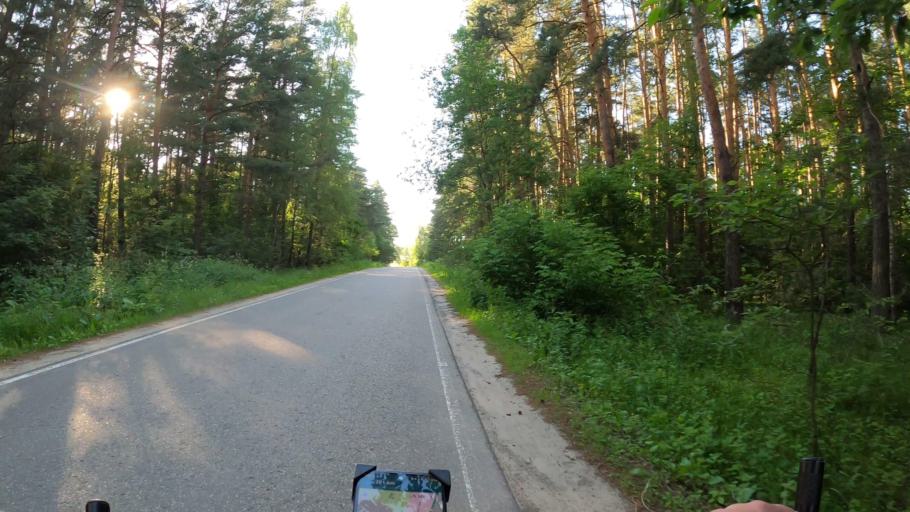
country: RU
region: Moskovskaya
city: Ashitkovo
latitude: 55.4434
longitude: 38.5980
